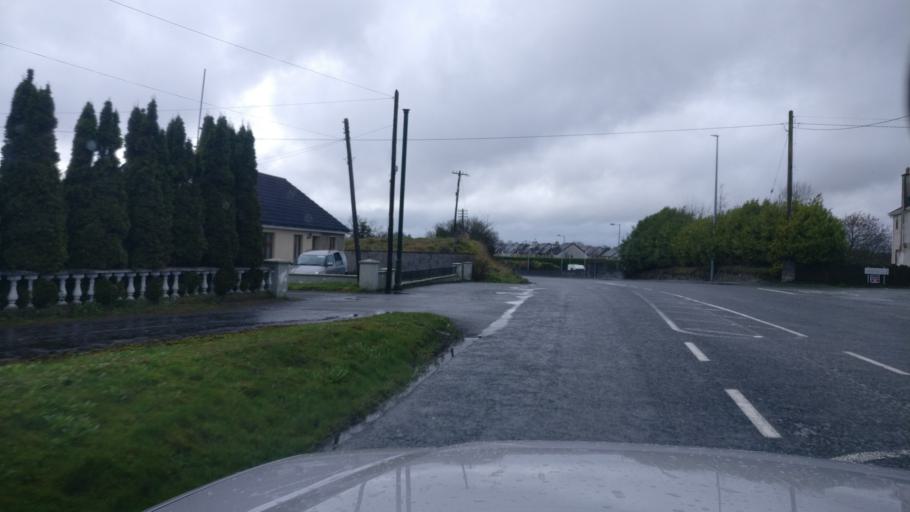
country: IE
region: Leinster
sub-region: An Iarmhi
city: Athlone
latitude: 53.4252
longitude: -8.0025
